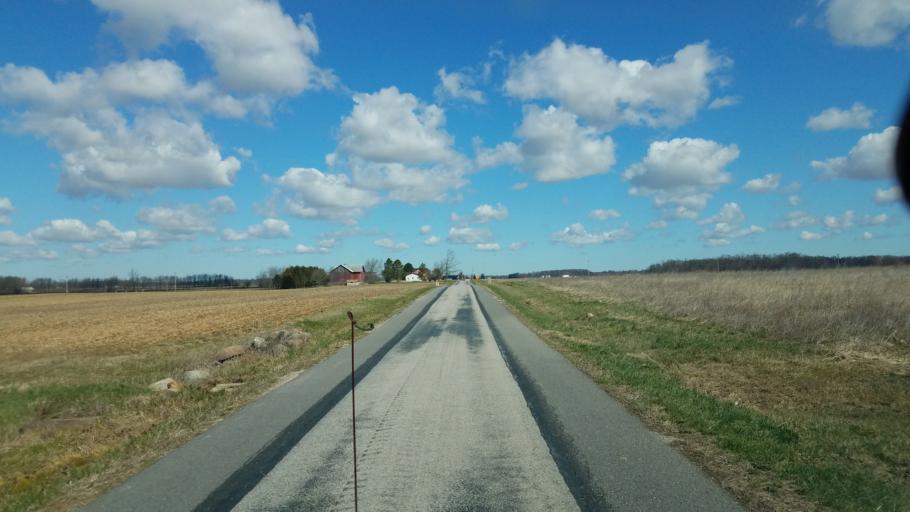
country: US
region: Ohio
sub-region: Sandusky County
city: Mount Carmel
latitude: 41.0915
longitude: -82.9382
